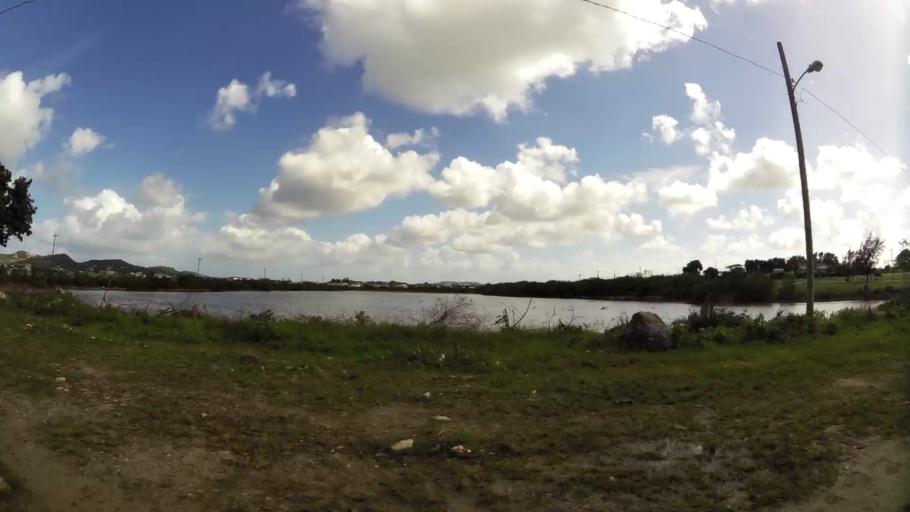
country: AG
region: Saint John
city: Saint John's
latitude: 17.1426
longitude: -61.8581
